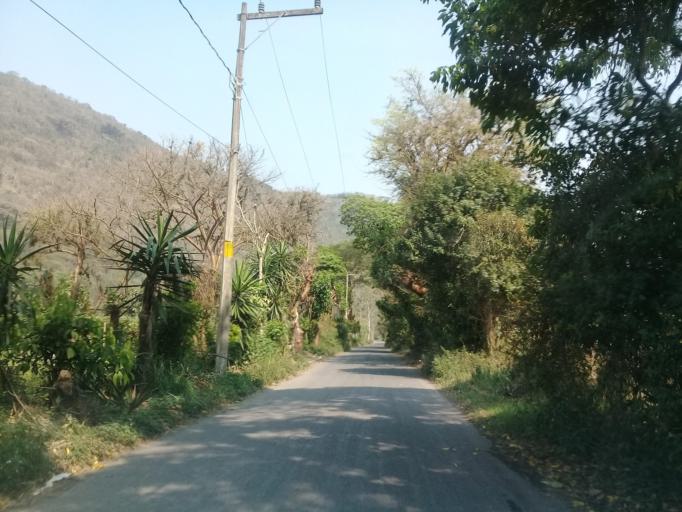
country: MX
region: Veracruz
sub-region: Ixtaczoquitlan
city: Campo Chico
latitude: 18.8339
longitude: -97.0208
